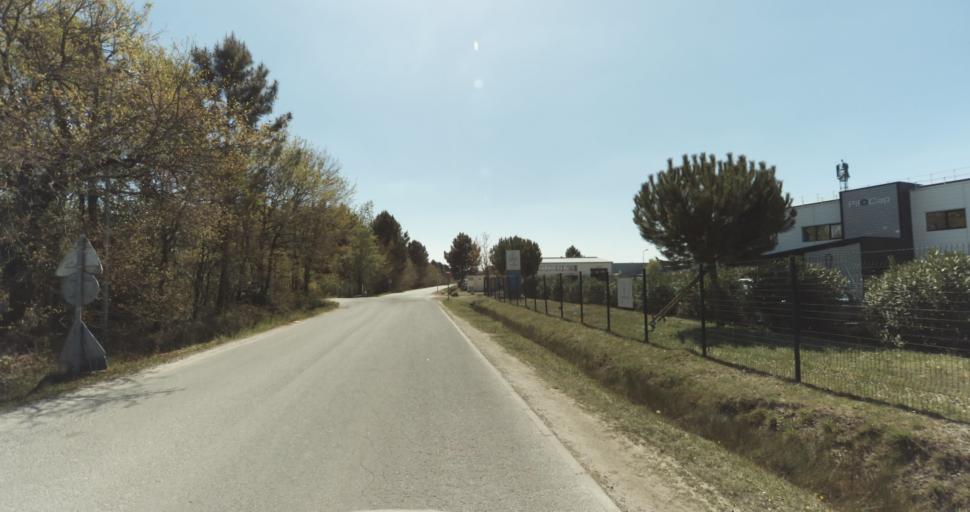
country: FR
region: Aquitaine
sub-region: Departement de la Gironde
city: Martignas-sur-Jalle
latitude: 44.8098
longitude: -0.7521
